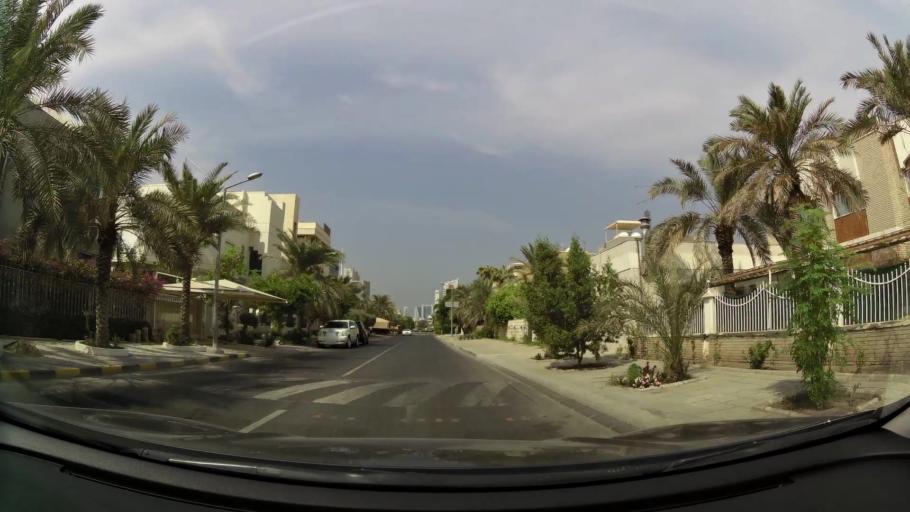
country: KW
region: Al Asimah
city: Ad Dasmah
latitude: 29.3541
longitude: 47.9890
